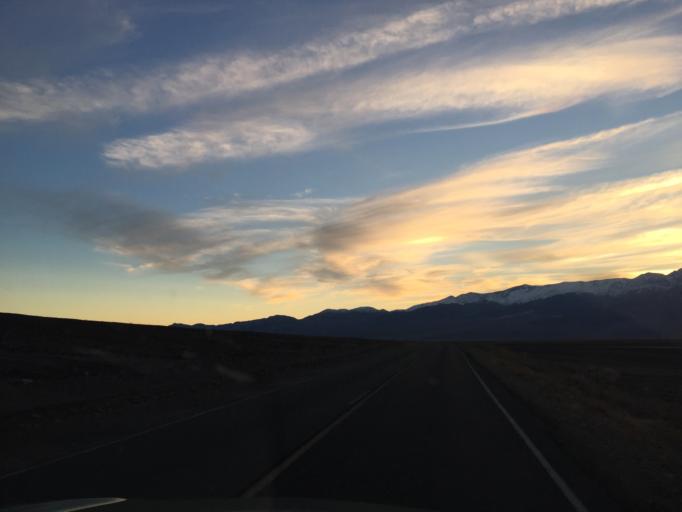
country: US
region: Nevada
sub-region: Nye County
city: Beatty
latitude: 36.2131
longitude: -116.7737
